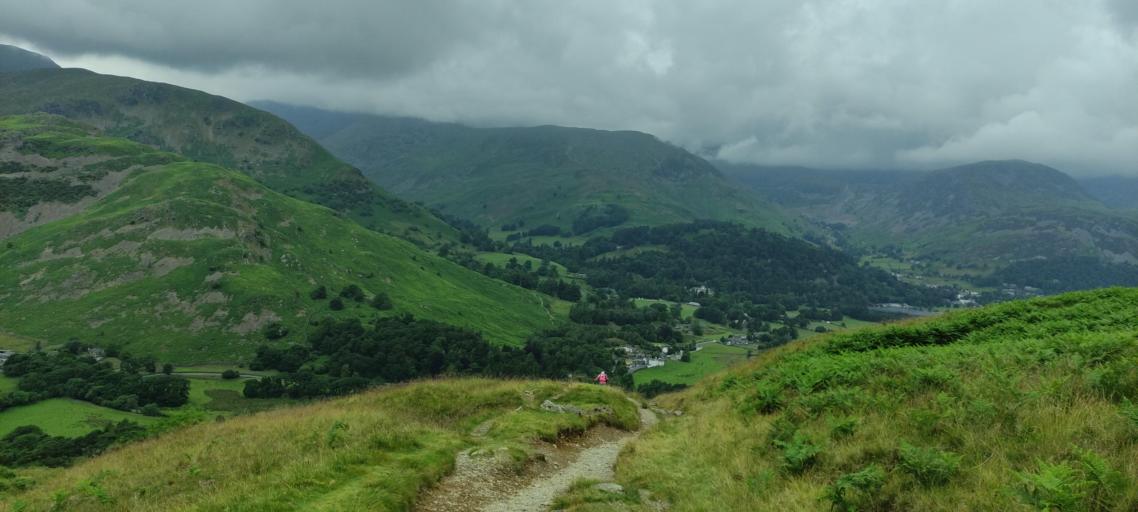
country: GB
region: England
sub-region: Cumbria
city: Ambleside
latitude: 54.5325
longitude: -2.9175
